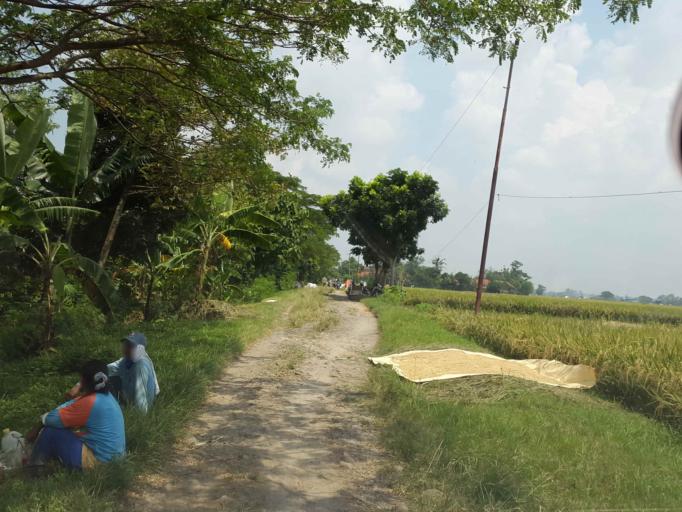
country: ID
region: Central Java
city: Dukuhkopi
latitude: -6.9611
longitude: 108.8247
